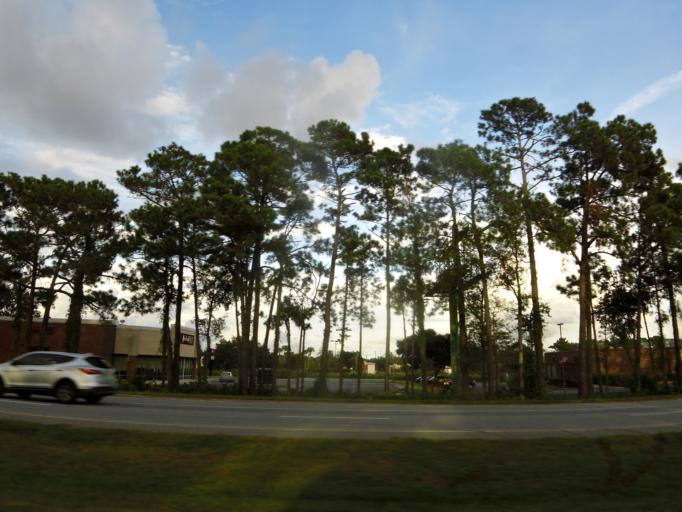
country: US
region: Georgia
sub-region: Glynn County
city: Country Club Estates
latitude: 31.2137
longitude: -81.4909
